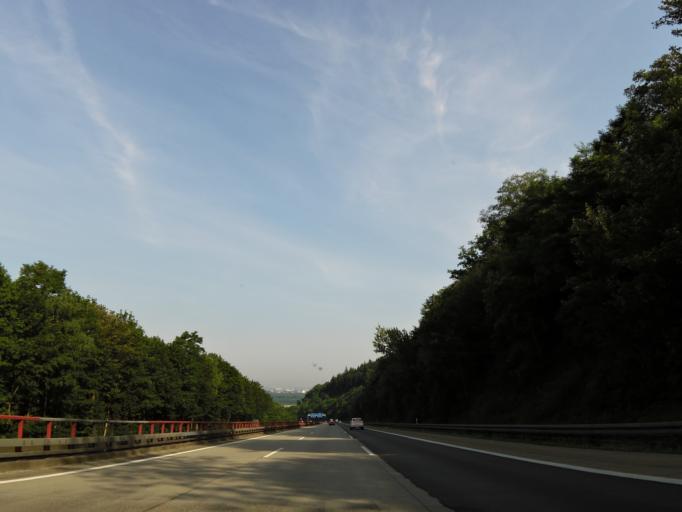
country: DE
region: Baden-Wuerttemberg
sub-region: Karlsruhe Region
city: Ettlingen
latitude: 48.9676
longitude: 8.4640
